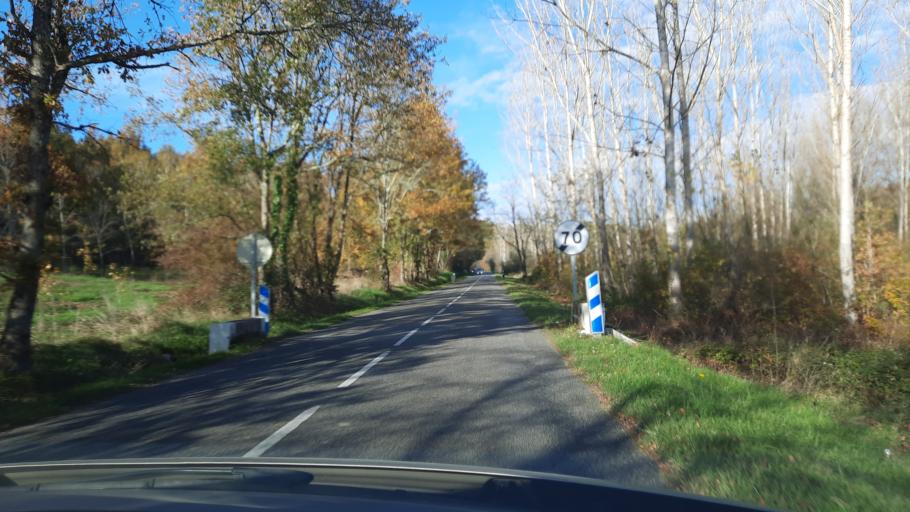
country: FR
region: Midi-Pyrenees
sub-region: Departement du Tarn-et-Garonne
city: Montauban
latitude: 44.1039
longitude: 1.3513
